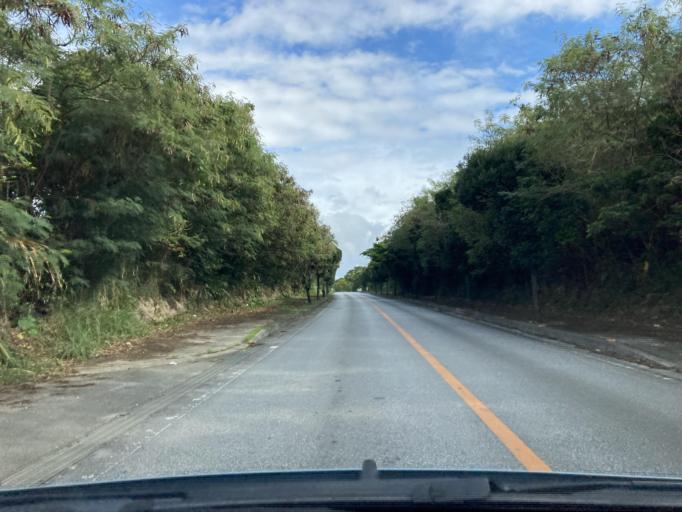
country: JP
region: Okinawa
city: Itoman
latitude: 26.1315
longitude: 127.7071
